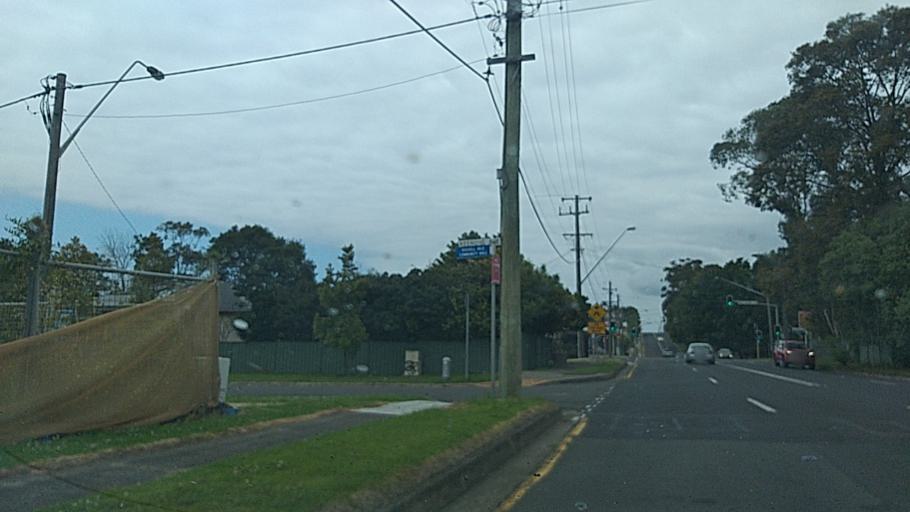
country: AU
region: New South Wales
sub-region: Wollongong
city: Corrimal
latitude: -34.3601
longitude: 150.8996
